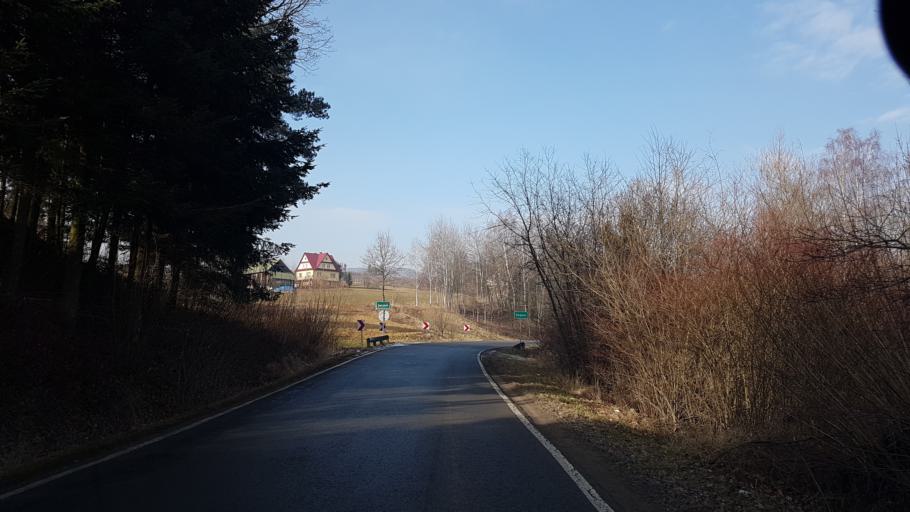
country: PL
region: Lesser Poland Voivodeship
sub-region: Powiat limanowski
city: Lukowica
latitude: 49.6043
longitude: 20.5187
